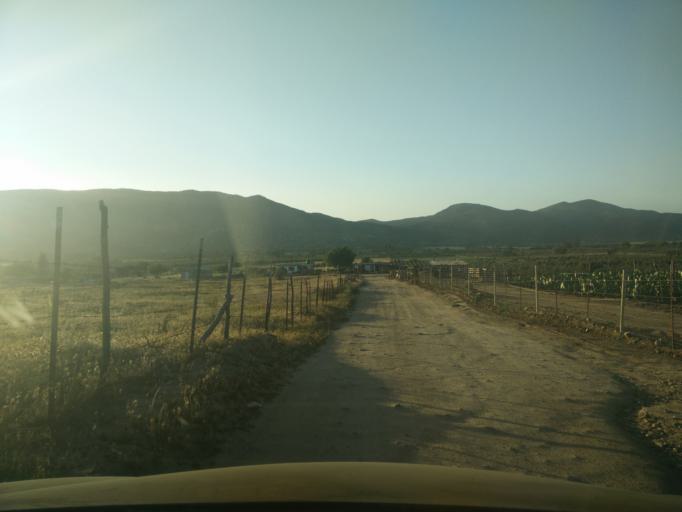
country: MX
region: Baja California
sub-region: Ensenada
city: Rancho Verde
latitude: 32.0466
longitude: -116.6453
